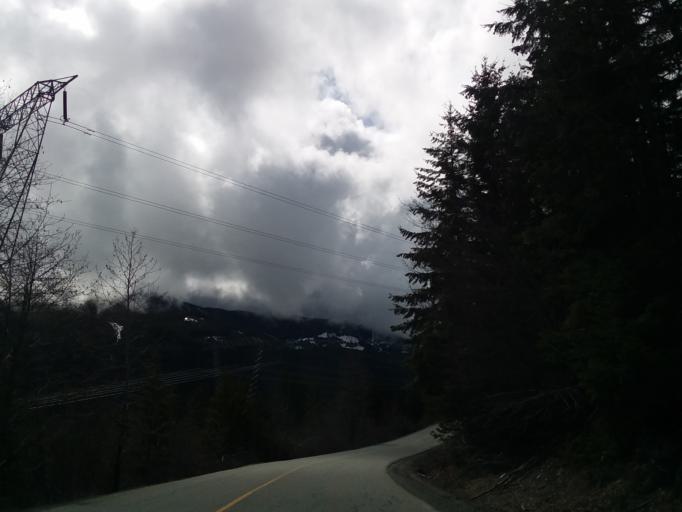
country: CA
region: British Columbia
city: Whistler
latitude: 50.1004
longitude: -123.0006
